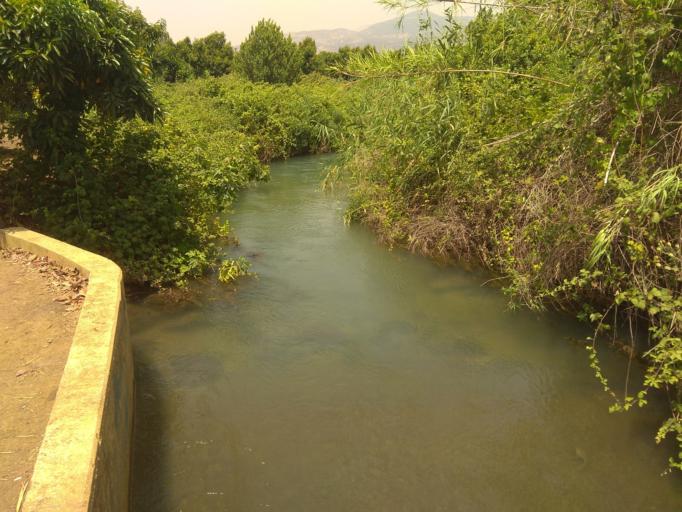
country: IL
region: Northern District
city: Qiryat Shemona
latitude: 33.2364
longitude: 35.6360
